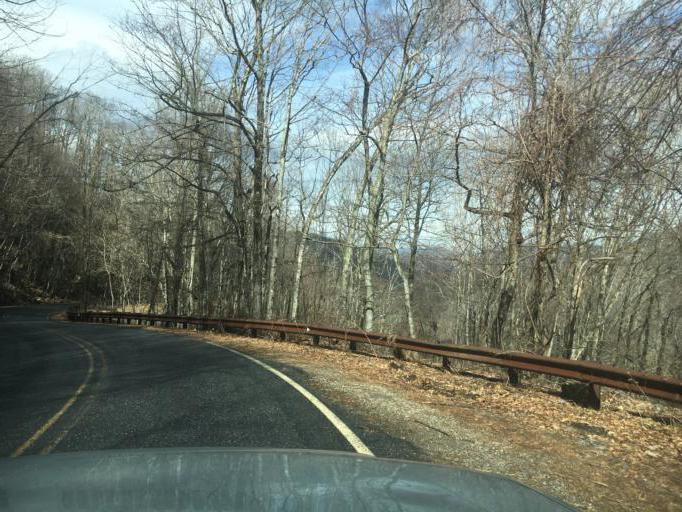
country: US
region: North Carolina
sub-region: Transylvania County
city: Brevard
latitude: 35.3690
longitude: -82.8038
